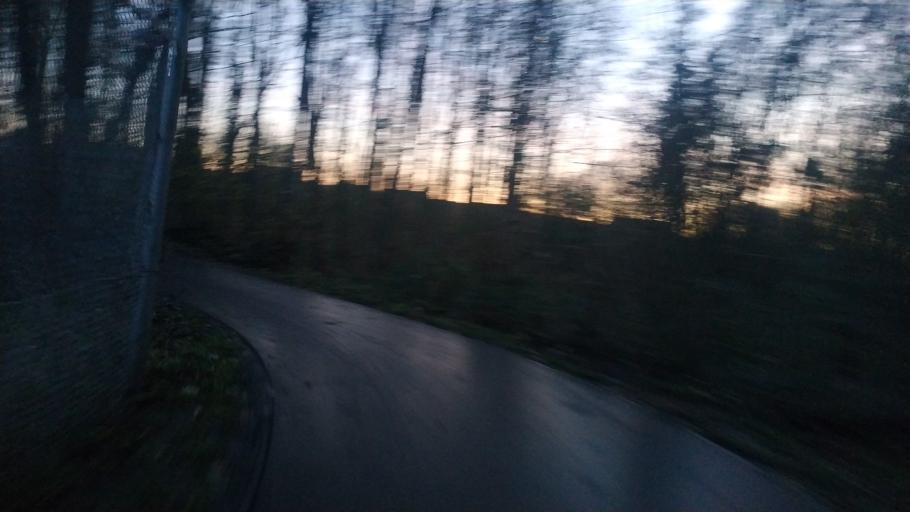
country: DE
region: North Rhine-Westphalia
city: Ibbenburen
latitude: 52.2670
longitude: 7.7119
